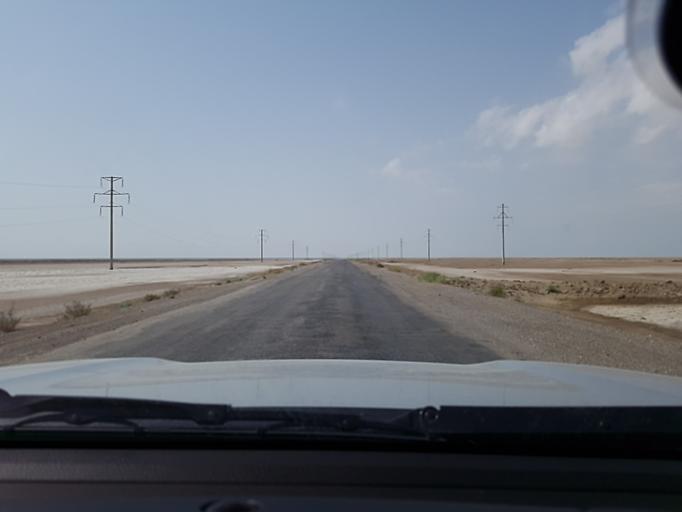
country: TM
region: Balkan
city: Gumdag
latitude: 39.0991
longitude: 54.5844
